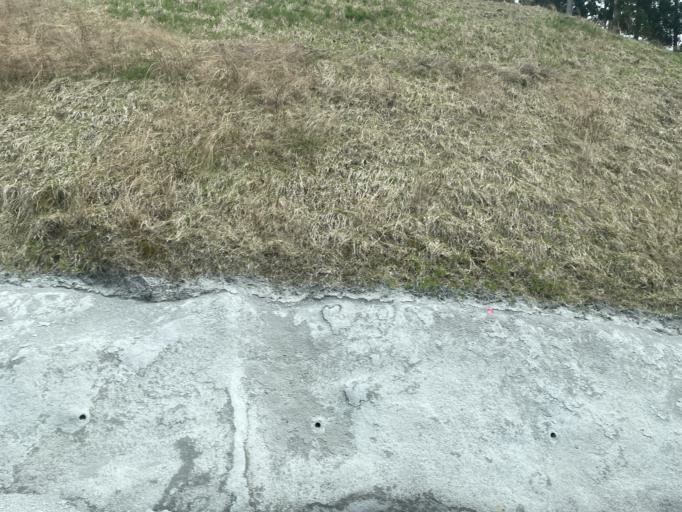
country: JP
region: Iwate
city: Ofunato
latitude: 38.9253
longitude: 141.6029
